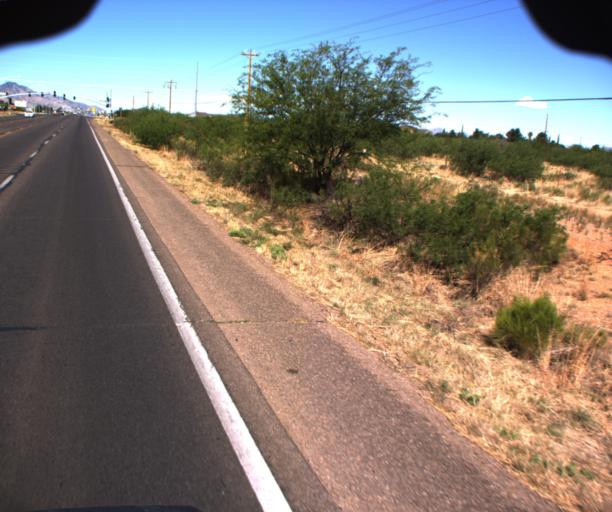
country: US
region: Arizona
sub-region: Cochise County
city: Sierra Vista
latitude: 31.5547
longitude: -110.2383
